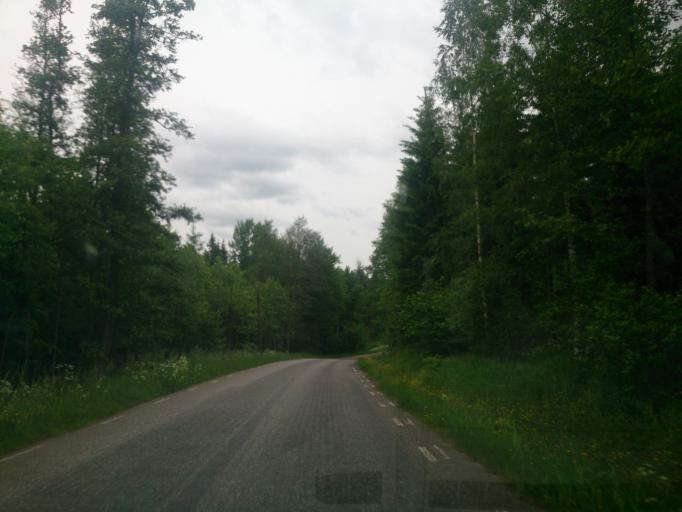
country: SE
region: OEstergoetland
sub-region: Soderkopings Kommun
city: Soederkoeping
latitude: 58.2991
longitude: 16.2542
